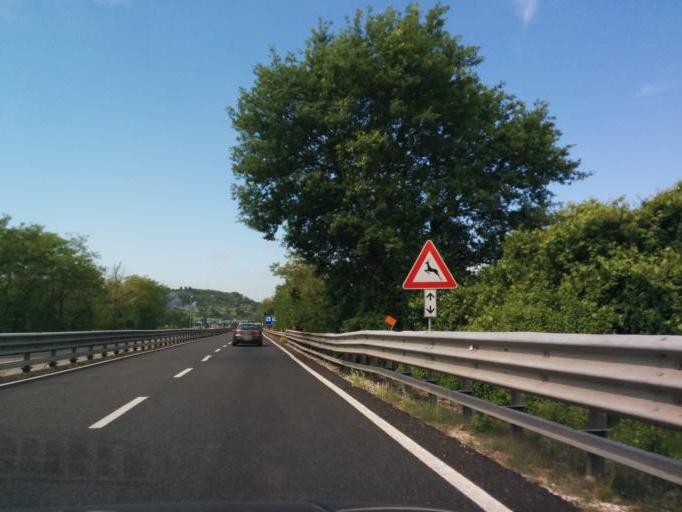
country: IT
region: Tuscany
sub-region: Provincia di Siena
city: Poggibonsi
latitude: 43.4909
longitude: 11.1742
